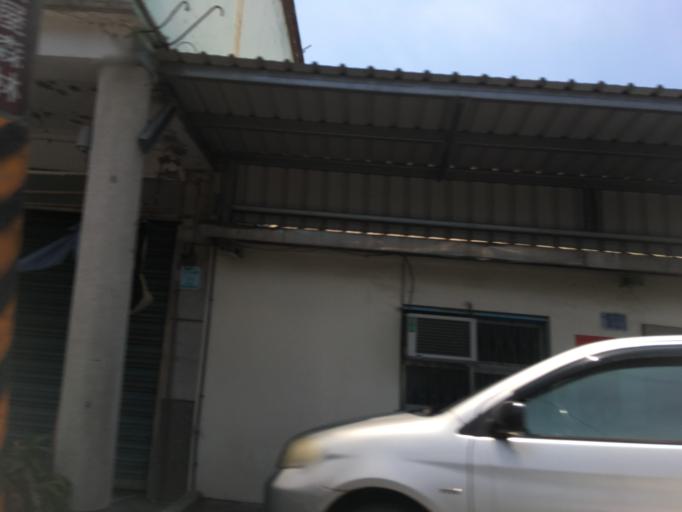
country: TW
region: Taiwan
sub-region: Yilan
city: Yilan
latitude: 24.6439
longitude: 121.7636
